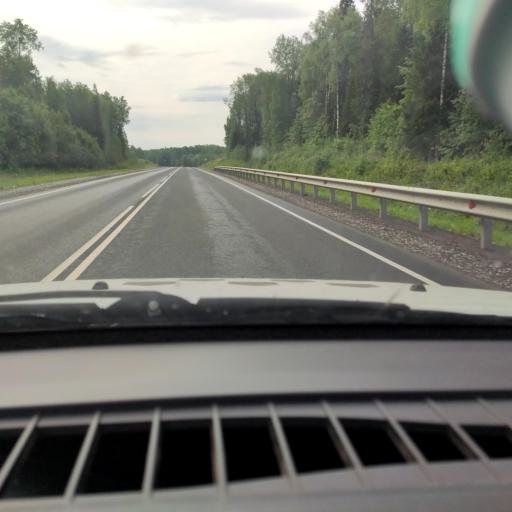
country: RU
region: Kirov
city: Kostino
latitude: 58.6594
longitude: 53.7679
